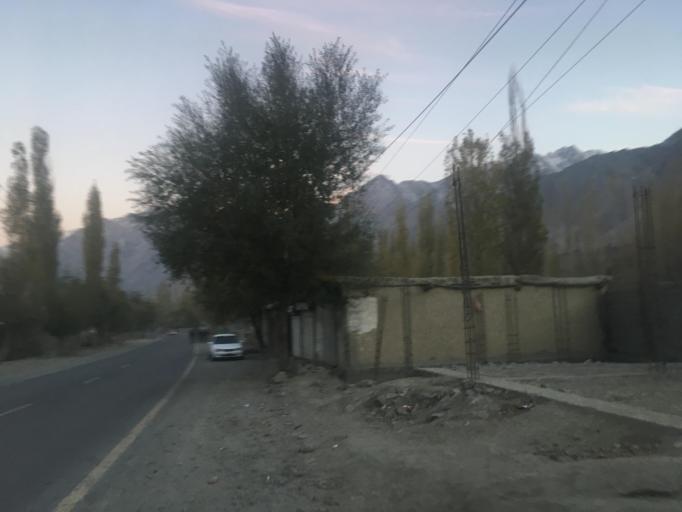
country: PK
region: Gilgit-Baltistan
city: Skardu
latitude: 35.3021
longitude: 75.5514
